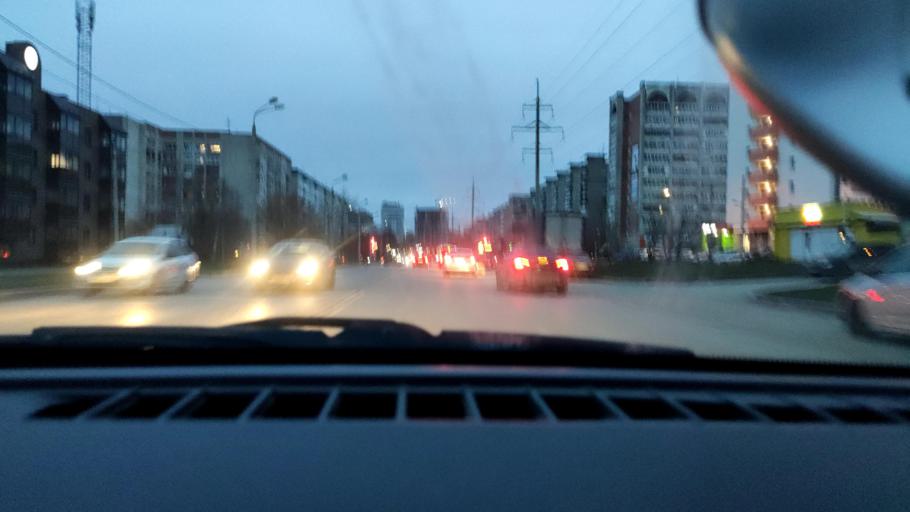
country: RU
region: Perm
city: Perm
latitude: 57.9768
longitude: 56.2023
